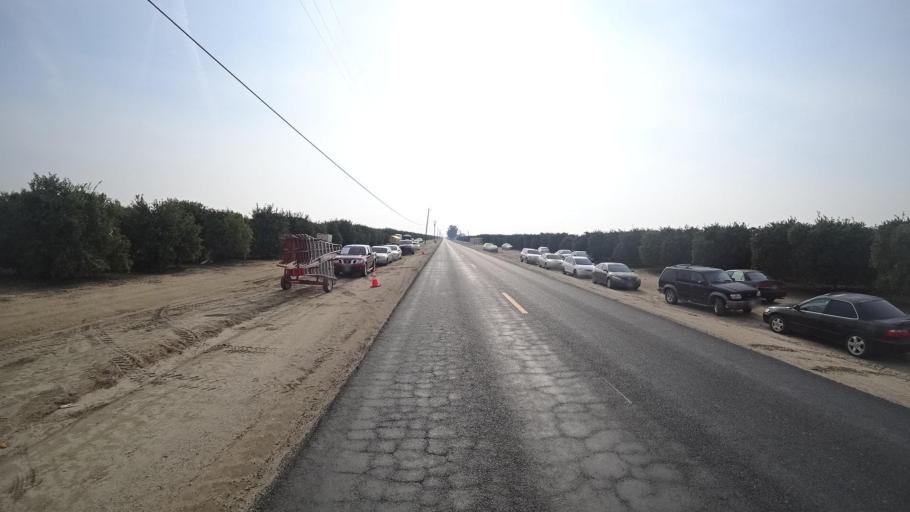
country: US
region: California
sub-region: Kern County
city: Arvin
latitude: 35.1485
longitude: -118.8508
